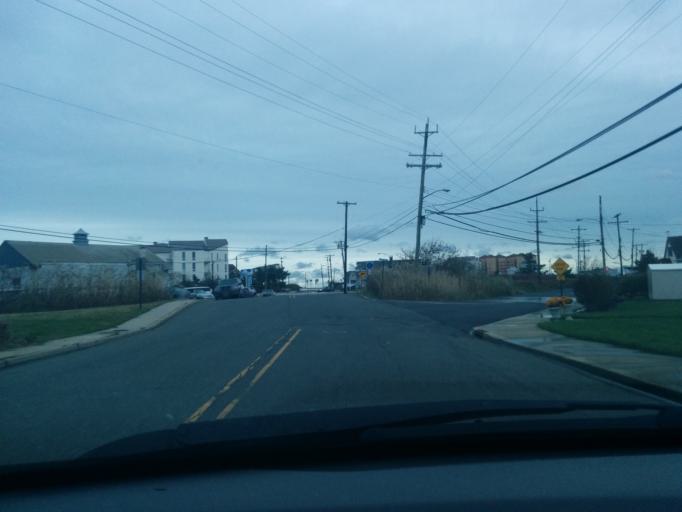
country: US
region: New Jersey
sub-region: Monmouth County
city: Monmouth Beach
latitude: 40.3233
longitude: -73.9779
